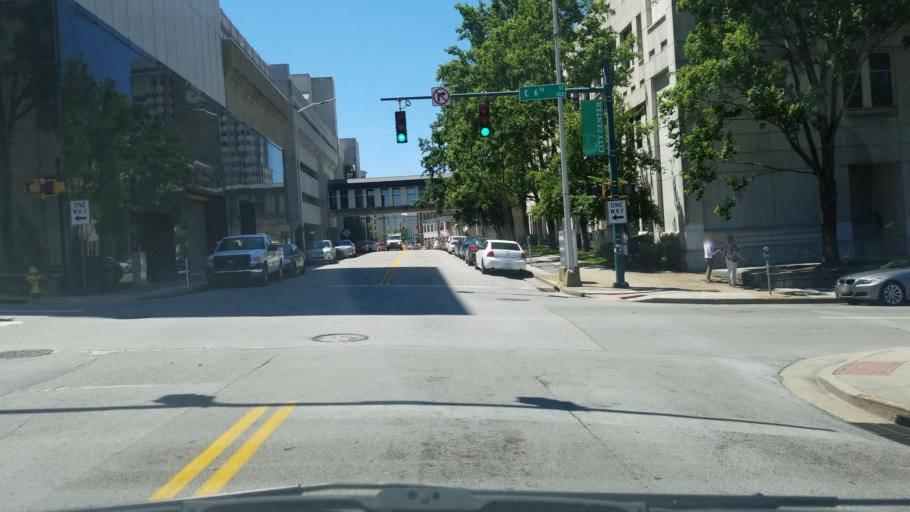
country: US
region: Tennessee
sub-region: Hamilton County
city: Chattanooga
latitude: 35.0498
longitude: -85.3085
